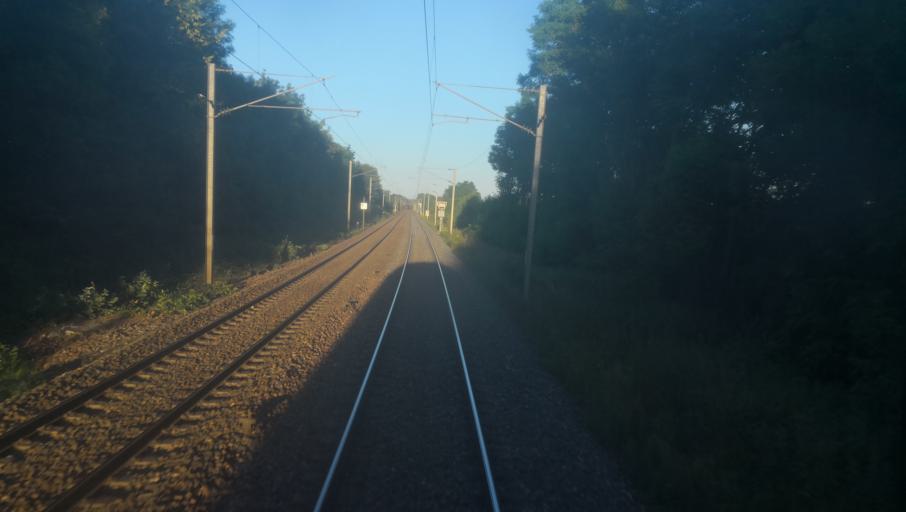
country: FR
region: Centre
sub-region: Departement du Cher
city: Cuffy
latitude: 46.8960
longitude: 3.0753
